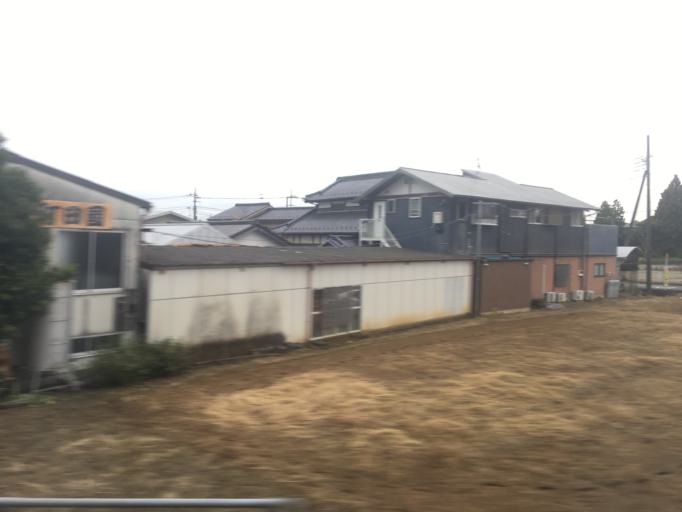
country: JP
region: Saitama
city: Hanno
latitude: 35.8634
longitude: 139.3308
